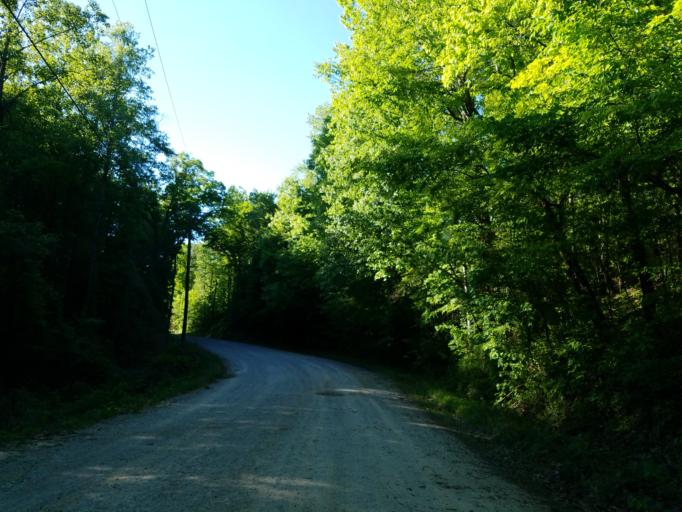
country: US
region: Georgia
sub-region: Gilmer County
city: Ellijay
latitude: 34.6380
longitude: -84.4969
